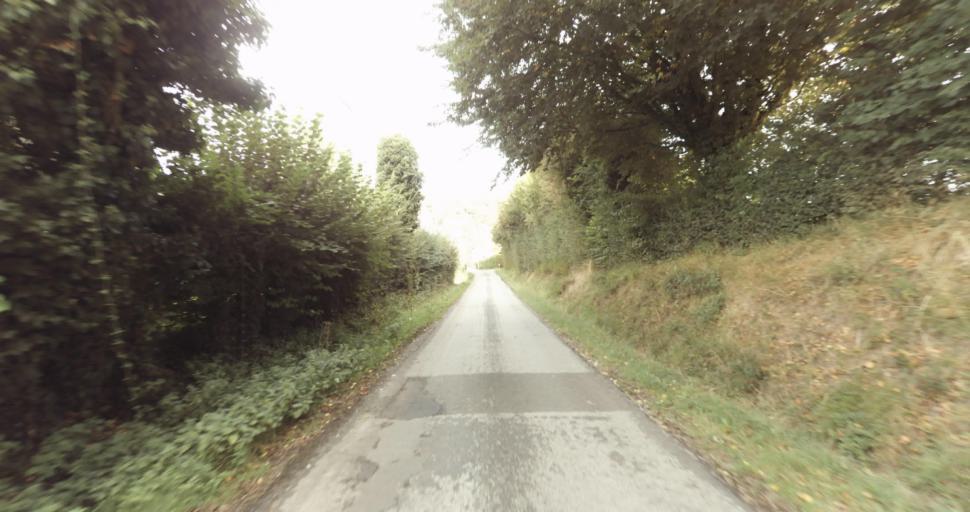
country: FR
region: Lower Normandy
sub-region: Departement de l'Orne
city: Gace
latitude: 48.8279
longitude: 0.2241
